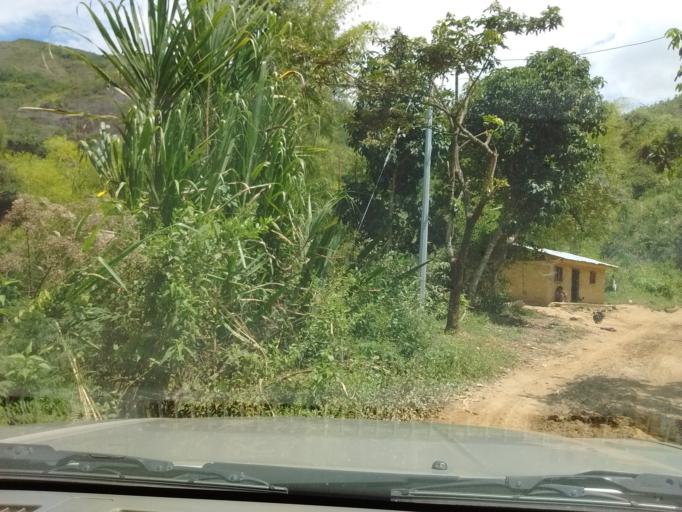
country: CO
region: Cauca
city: Morales
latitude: 2.6701
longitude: -76.7642
